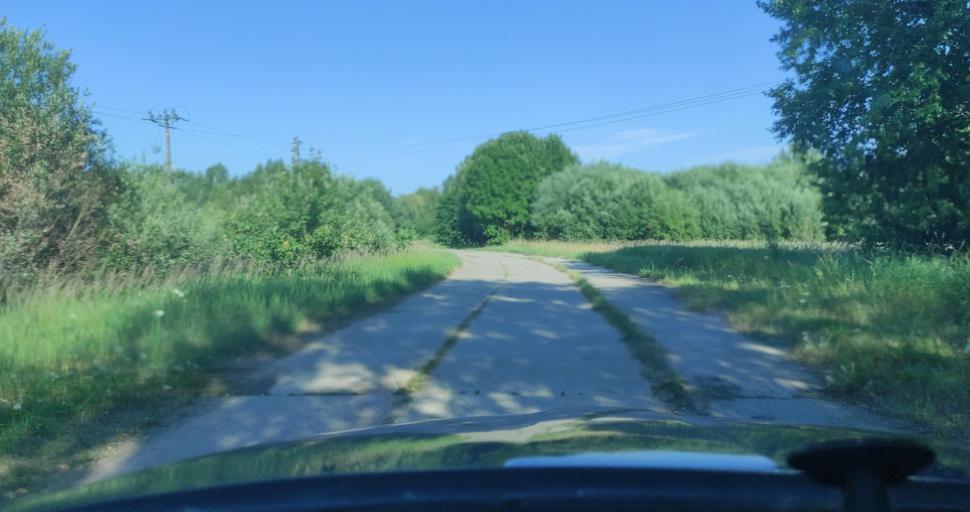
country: LV
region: Skrunda
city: Skrunda
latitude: 56.6790
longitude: 22.0052
